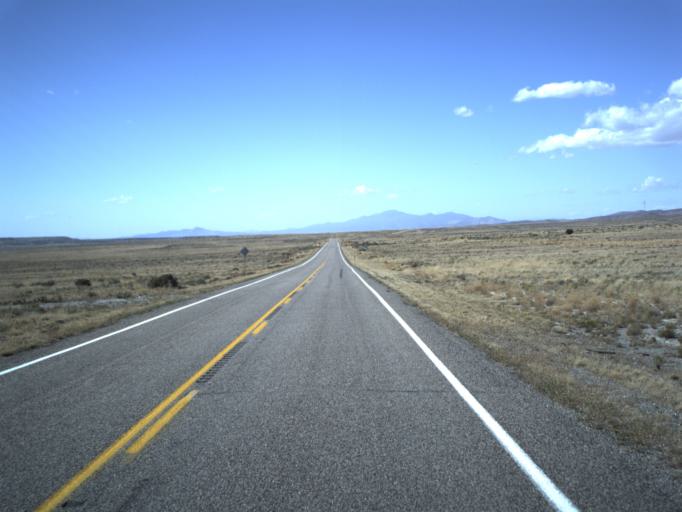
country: US
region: Utah
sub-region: Beaver County
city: Milford
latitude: 38.8225
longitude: -112.8550
